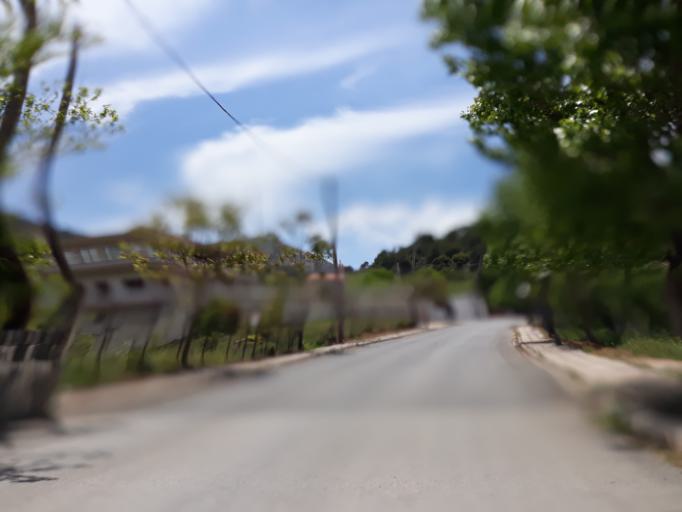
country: GR
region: Attica
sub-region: Nomarchia Dytikis Attikis
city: Magoula
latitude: 38.1736
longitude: 23.5469
